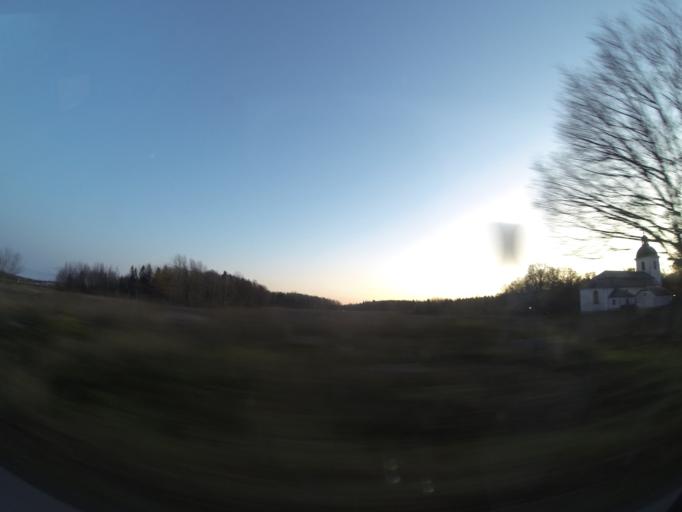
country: SE
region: OErebro
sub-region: Lindesbergs Kommun
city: Fellingsbro
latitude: 59.3258
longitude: 15.4791
